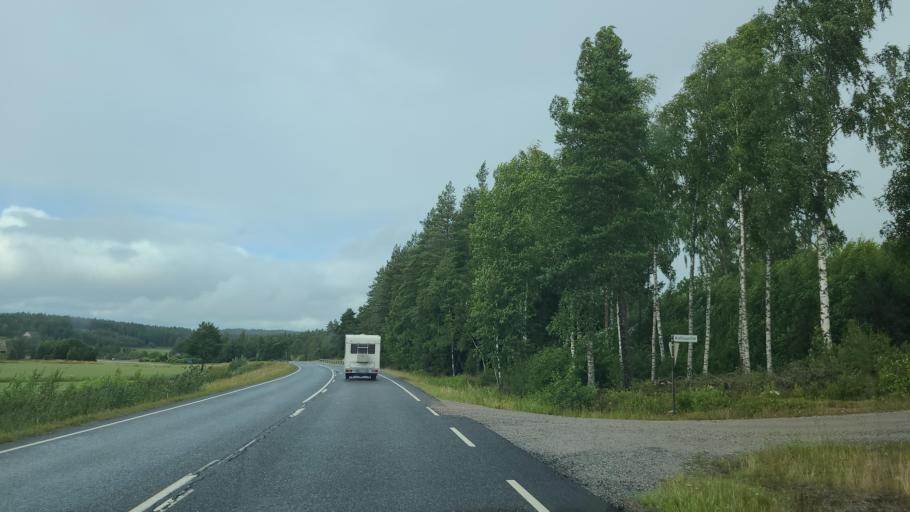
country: FI
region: Varsinais-Suomi
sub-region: Turku
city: Sauvo
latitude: 60.3267
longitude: 22.7143
